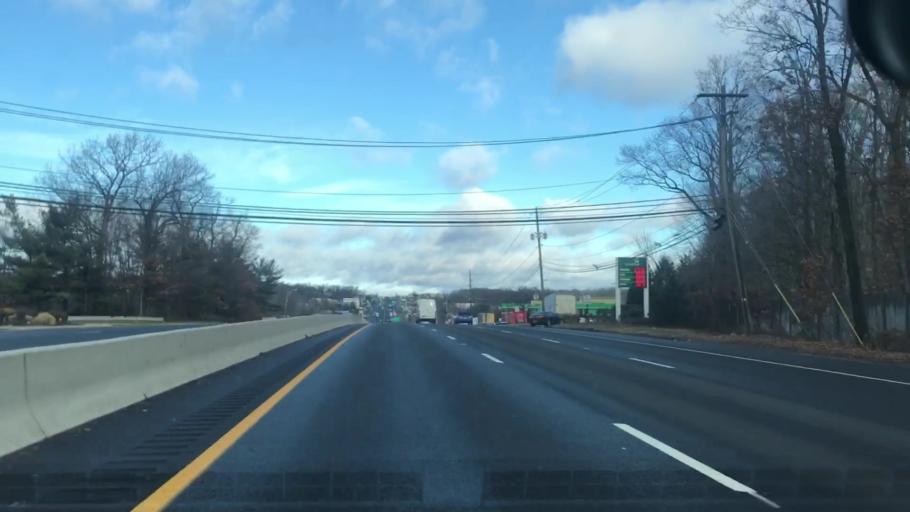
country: US
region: New Jersey
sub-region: Bergen County
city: Allendale
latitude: 41.0423
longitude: -74.1147
